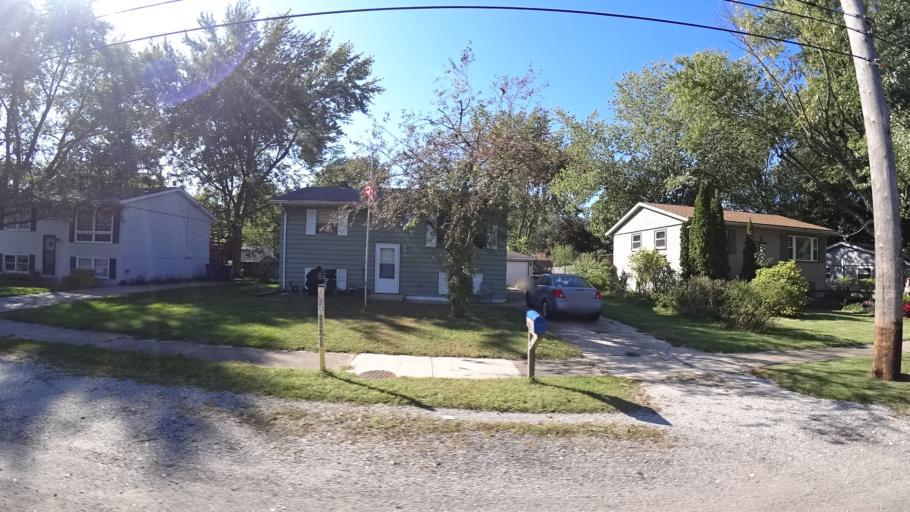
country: US
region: Indiana
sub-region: LaPorte County
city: Michigan City
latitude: 41.6906
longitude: -86.9035
